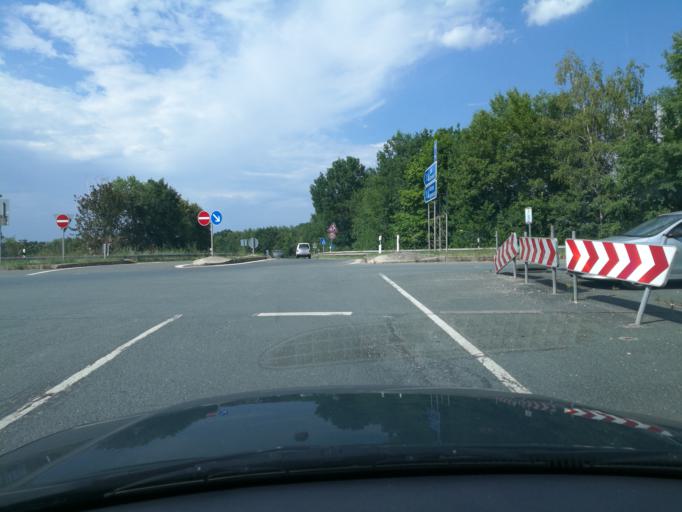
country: DE
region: Bavaria
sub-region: Regierungsbezirk Mittelfranken
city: Erlangen
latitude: 49.5406
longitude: 10.9948
